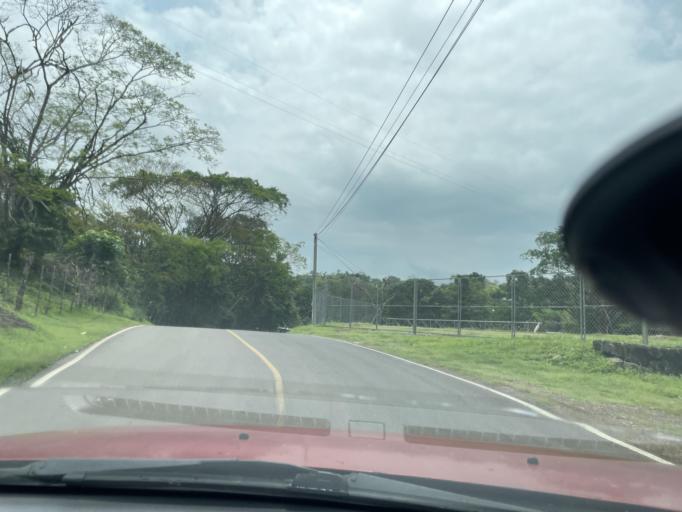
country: SV
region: La Union
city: Santa Rosa de Lima
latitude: 13.6491
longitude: -87.8466
